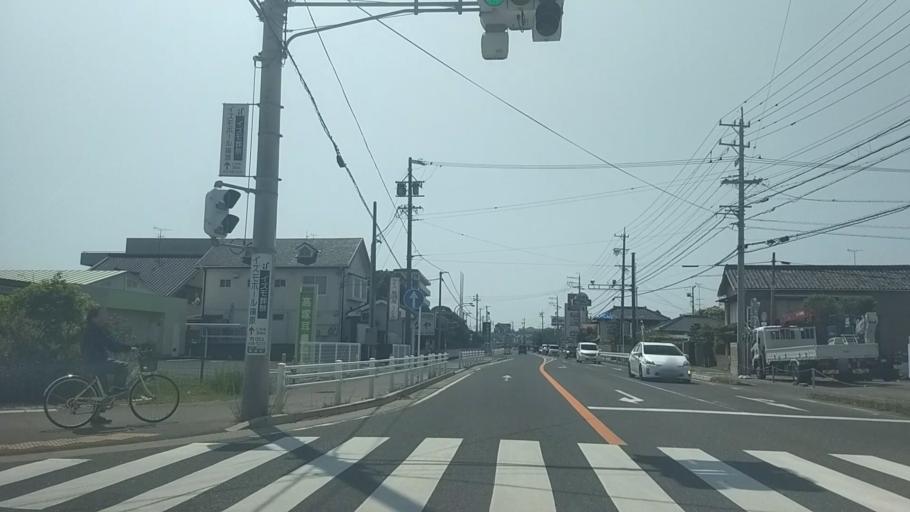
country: JP
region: Shizuoka
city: Hamamatsu
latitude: 34.6878
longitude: 137.6780
